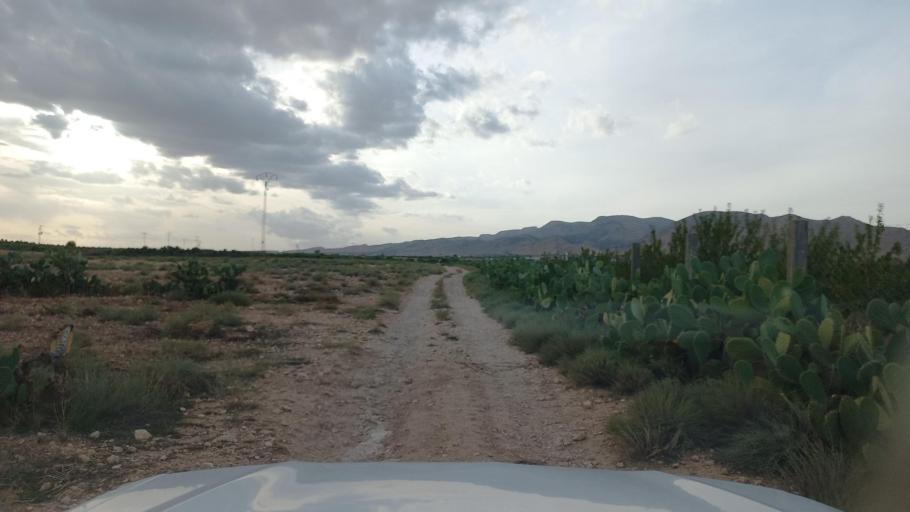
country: TN
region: Al Qasrayn
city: Sbiba
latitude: 35.4409
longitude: 9.0912
